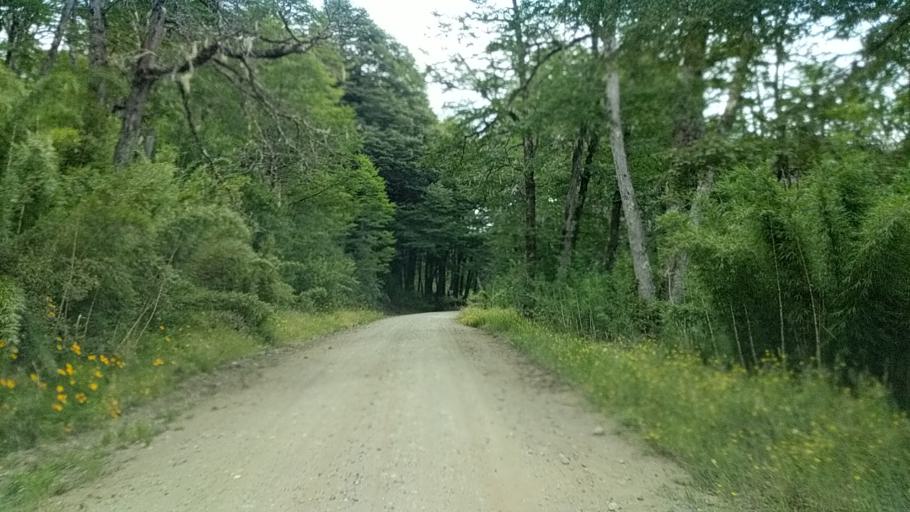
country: AR
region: Neuquen
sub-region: Departamento de Lacar
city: San Martin de los Andes
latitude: -39.8271
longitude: -71.6379
